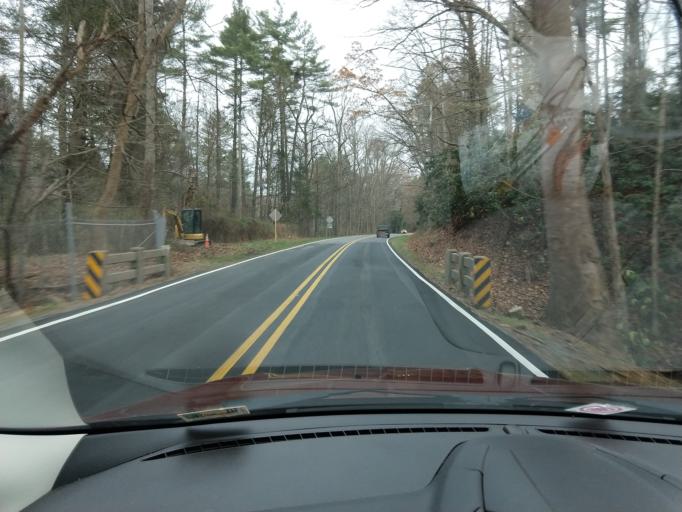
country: US
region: Virginia
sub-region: City of Covington
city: Covington
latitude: 37.7561
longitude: -80.1324
